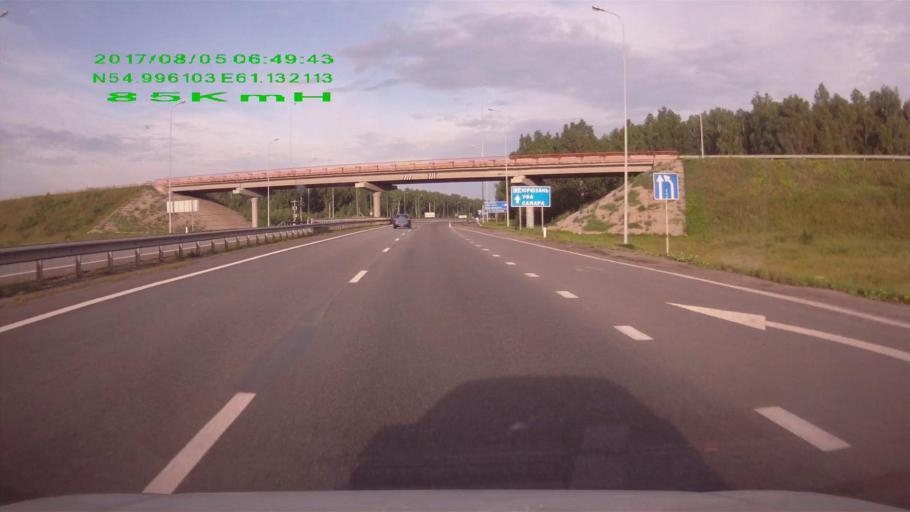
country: RU
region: Chelyabinsk
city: Poletayevo
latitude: 54.9960
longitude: 61.1319
